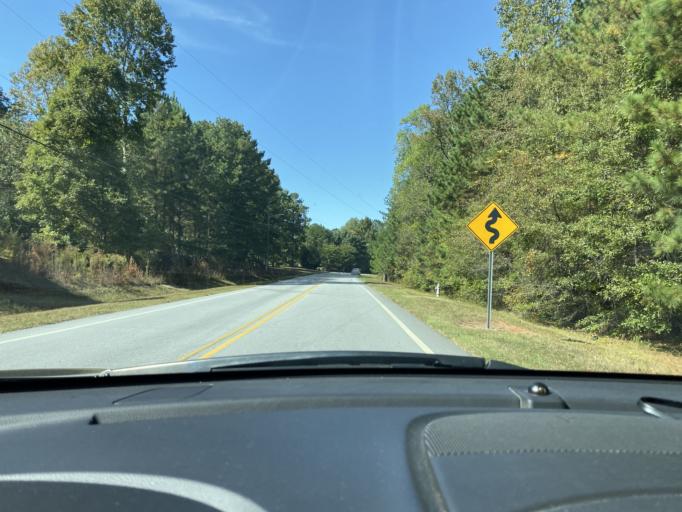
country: US
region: Georgia
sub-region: Gwinnett County
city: Grayson
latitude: 33.8984
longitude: -83.9122
